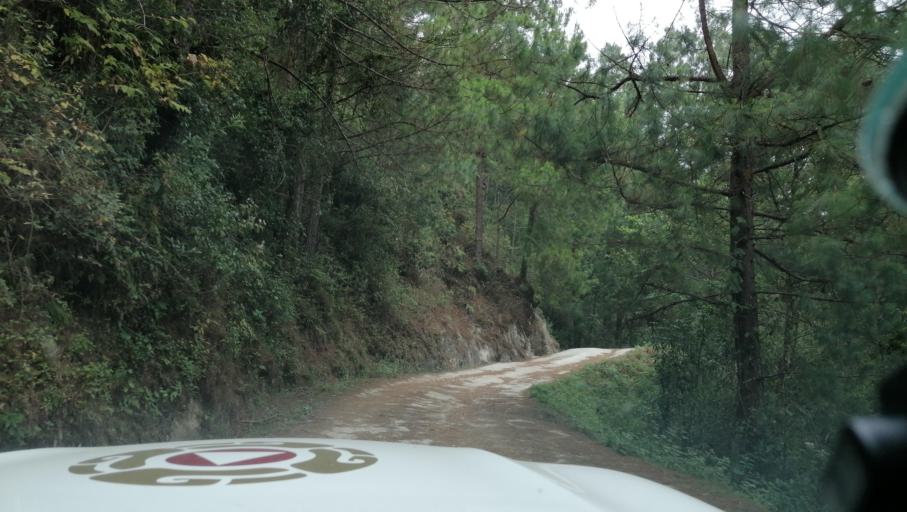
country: MX
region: Chiapas
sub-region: Tapachula
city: Canton Villaflor
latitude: 15.1982
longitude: -92.2339
